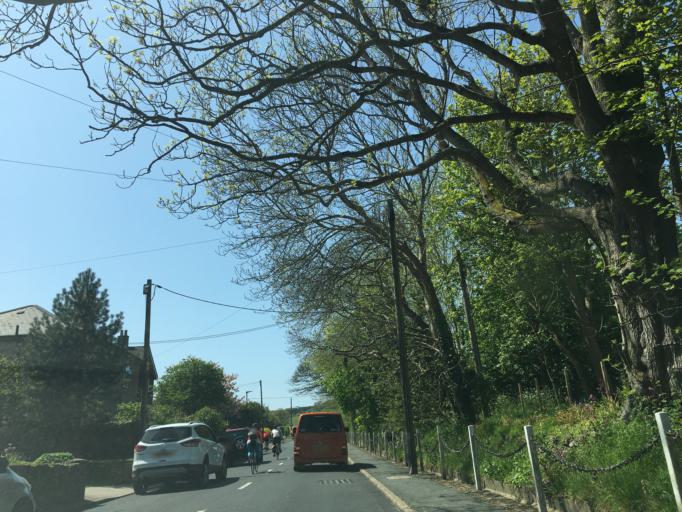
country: GB
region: England
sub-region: Isle of Wight
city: Niton
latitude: 50.5876
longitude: -1.2884
